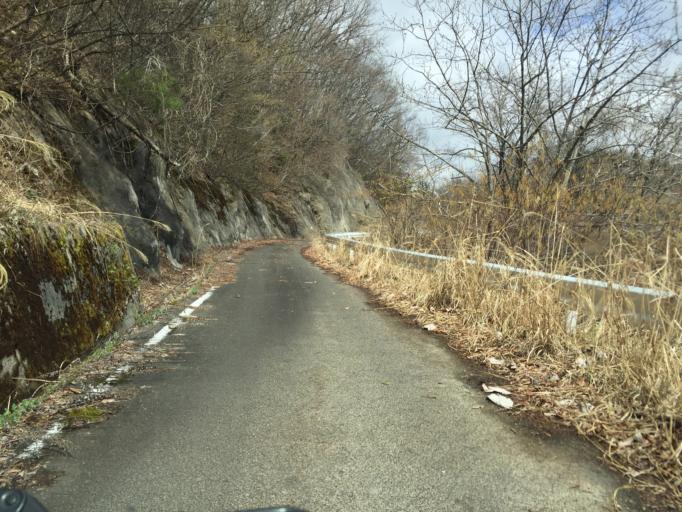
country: JP
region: Fukushima
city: Fukushima-shi
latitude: 37.8580
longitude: 140.4233
